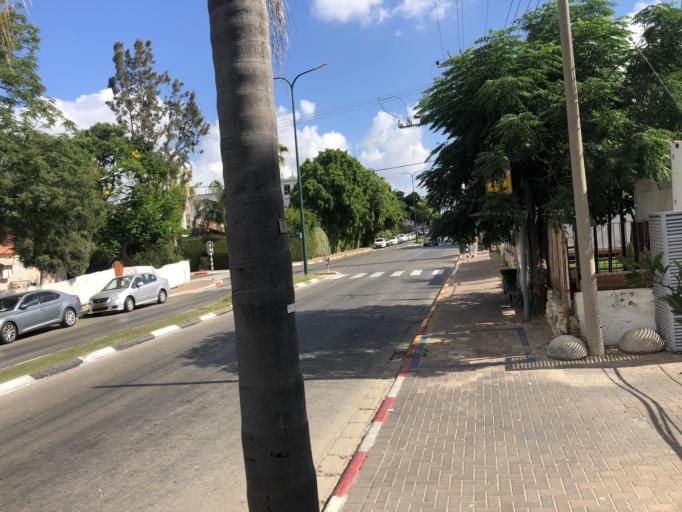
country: IL
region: Central District
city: Yehud
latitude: 32.0288
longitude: 34.8972
